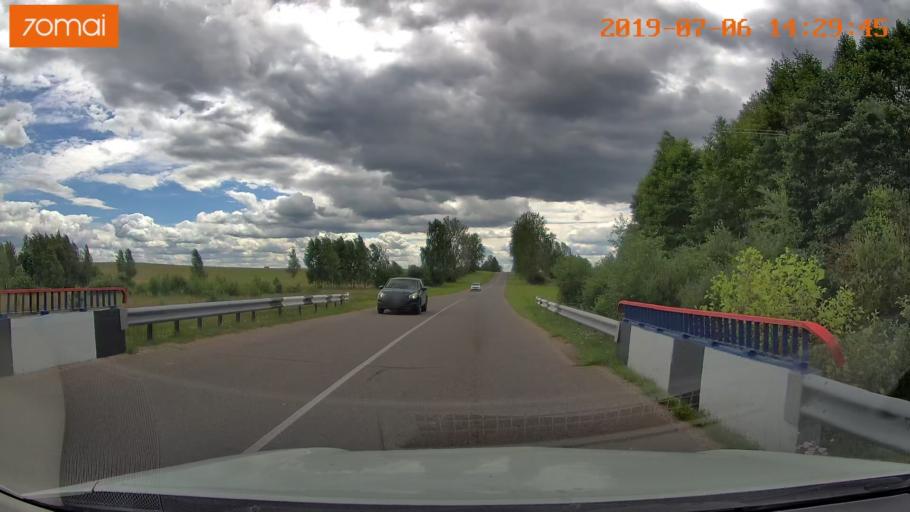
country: BY
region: Minsk
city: Ivyanyets
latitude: 53.9307
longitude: 26.7936
